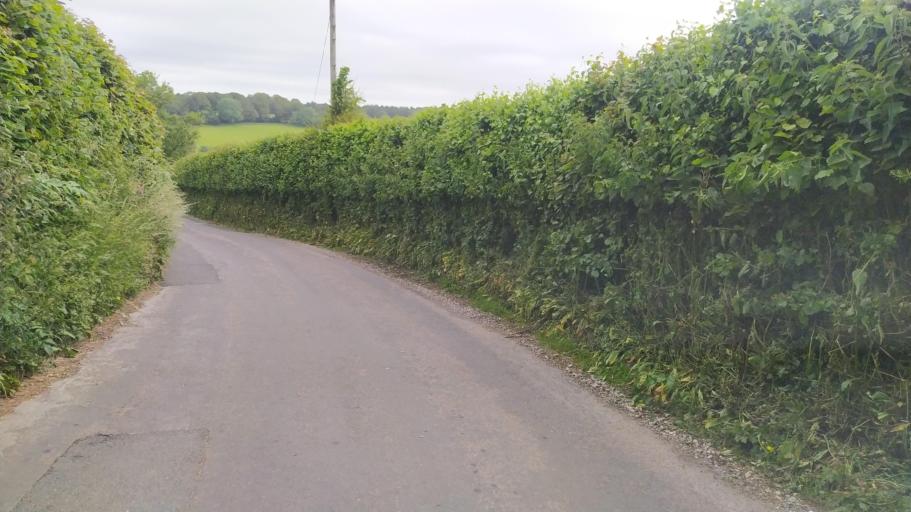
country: GB
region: England
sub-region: Somerset
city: Yeovil
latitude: 50.8359
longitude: -2.6062
